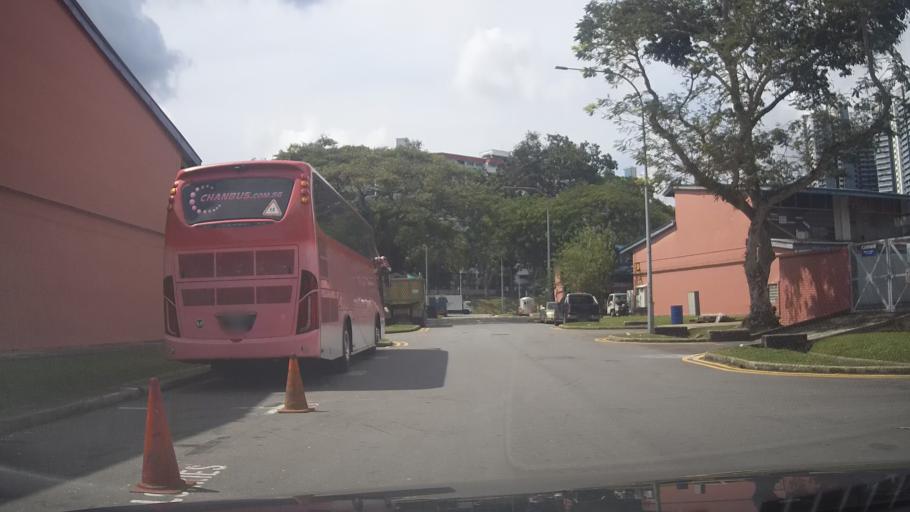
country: MY
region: Johor
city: Johor Bahru
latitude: 1.4408
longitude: 103.7820
